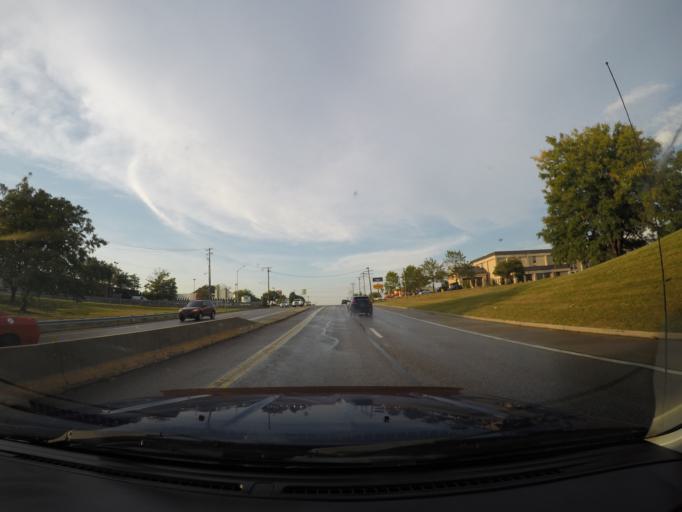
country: US
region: Missouri
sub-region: Saint Louis County
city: Sunset Hills
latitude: 38.5557
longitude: -90.4070
